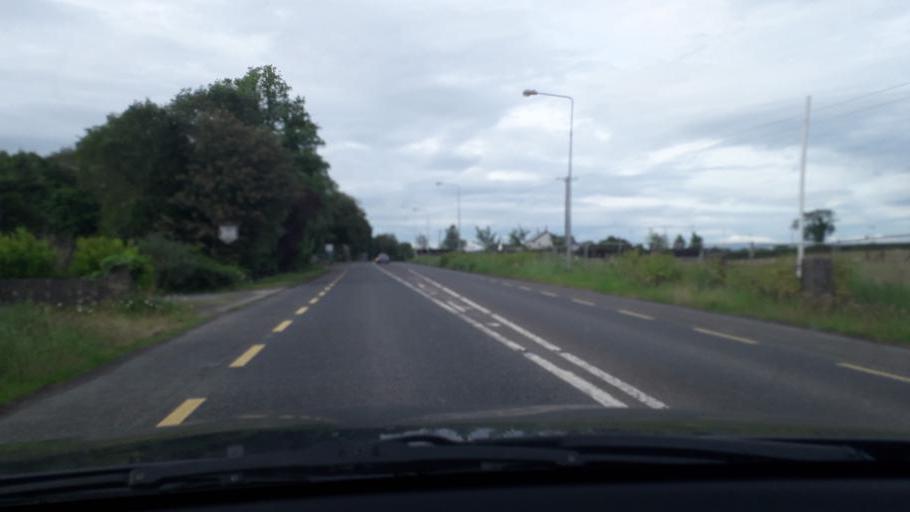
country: IE
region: Leinster
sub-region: County Carlow
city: Carlow
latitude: 52.8120
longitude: -6.9520
